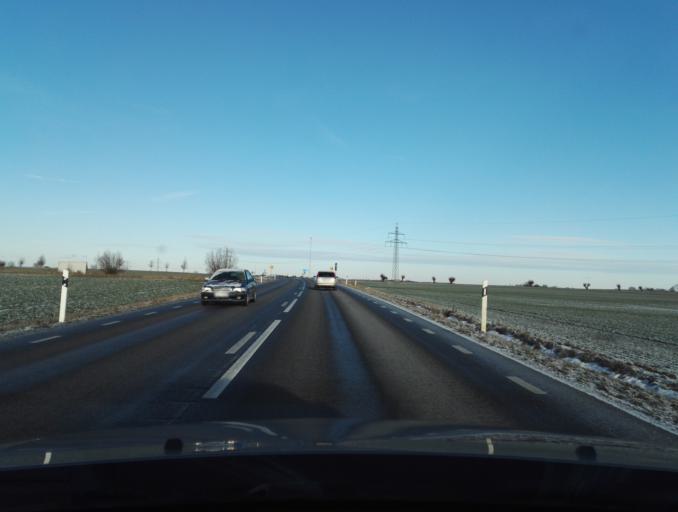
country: SE
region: Skane
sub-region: Trelleborgs Kommun
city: Trelleborg
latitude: 55.4098
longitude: 13.1660
